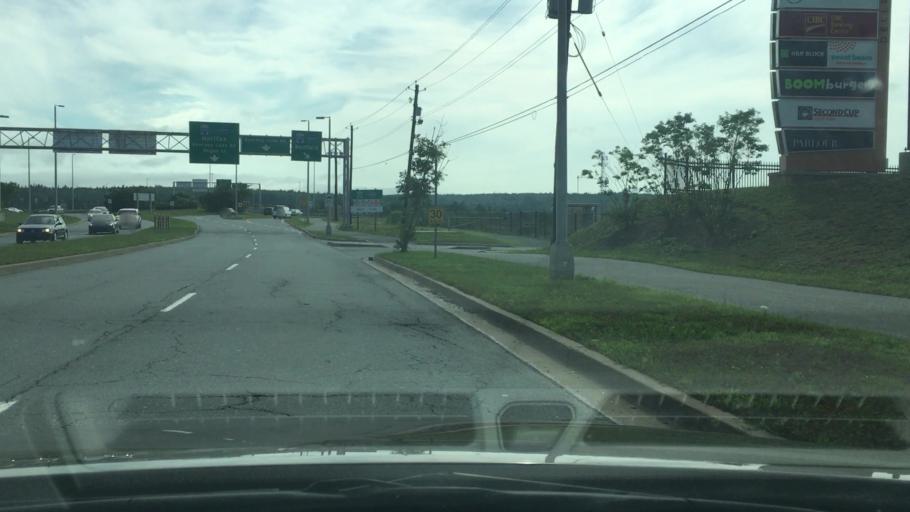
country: CA
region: Nova Scotia
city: Dartmouth
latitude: 44.7003
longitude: -63.6881
